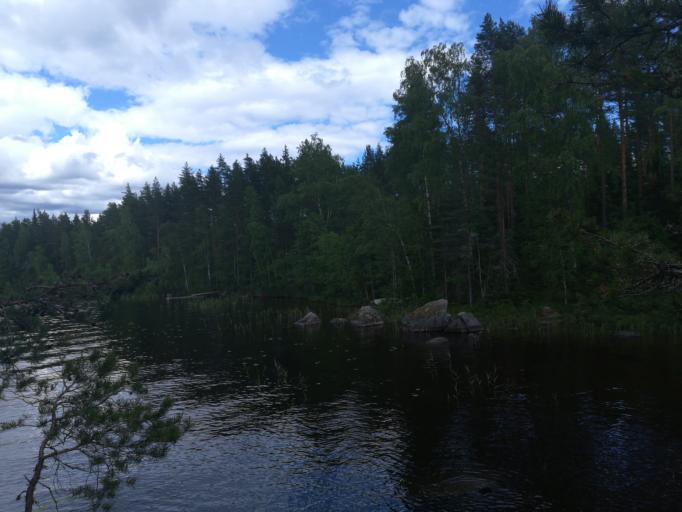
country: FI
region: Southern Savonia
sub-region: Mikkeli
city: Mikkeli
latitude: 61.6913
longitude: 27.0339
